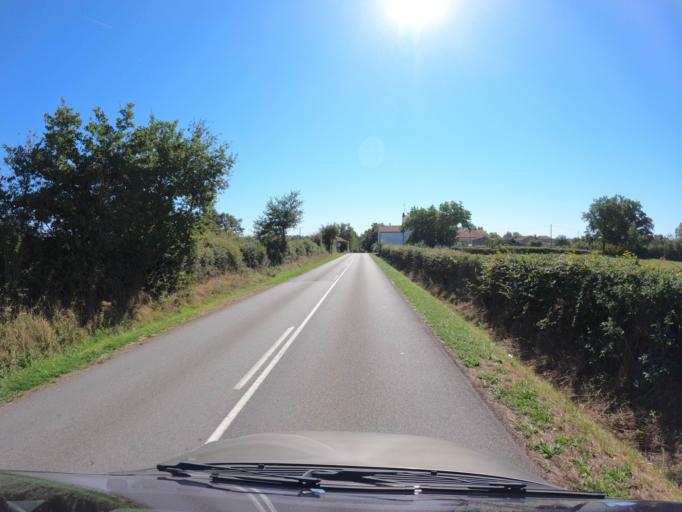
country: FR
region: Limousin
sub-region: Departement de la Haute-Vienne
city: Le Dorat
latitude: 46.2405
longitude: 1.0540
